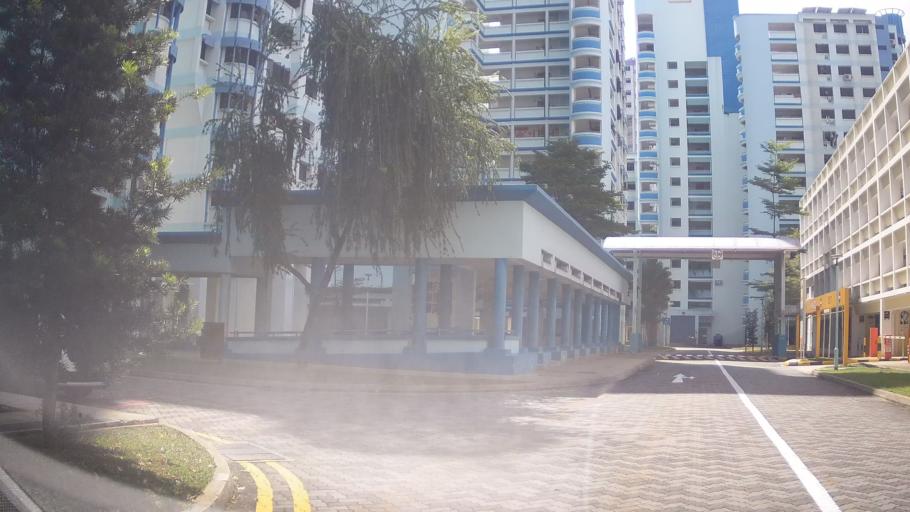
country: MY
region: Johor
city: Johor Bahru
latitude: 1.3389
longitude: 103.7230
